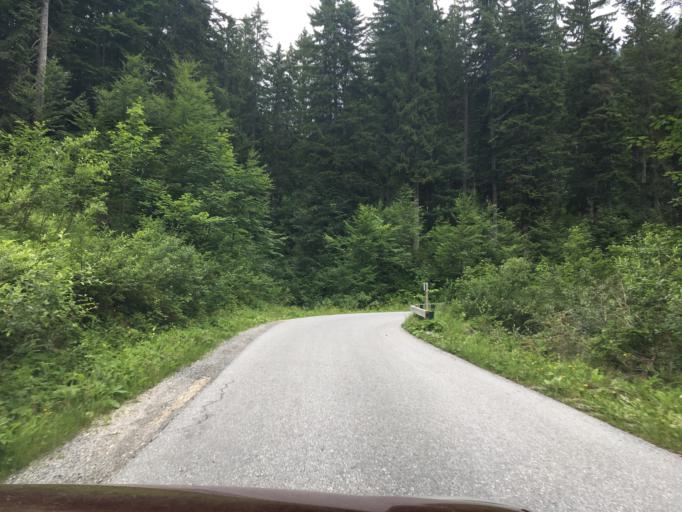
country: AT
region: Salzburg
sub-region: Politischer Bezirk Hallein
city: Abtenau
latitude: 47.6143
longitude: 13.3828
